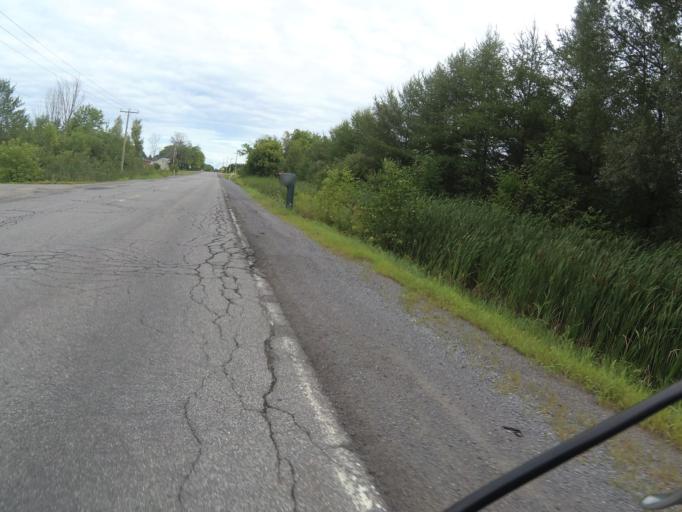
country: CA
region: Ontario
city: Bourget
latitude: 45.3640
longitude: -75.2634
